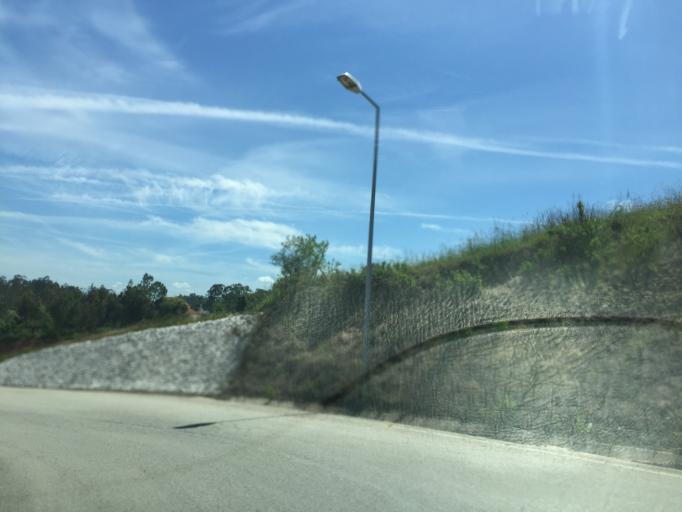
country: PT
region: Leiria
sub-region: Pombal
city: Lourical
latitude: 40.0664
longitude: -8.7289
